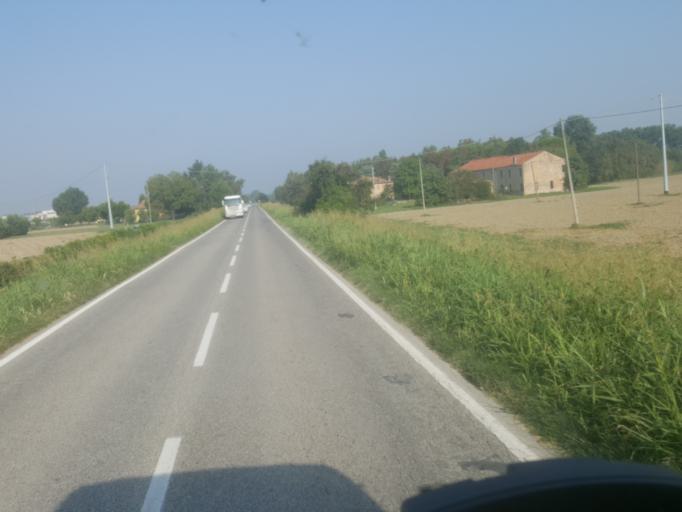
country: IT
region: Emilia-Romagna
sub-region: Provincia di Ravenna
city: Lavezzola
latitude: 44.5666
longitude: 11.8968
